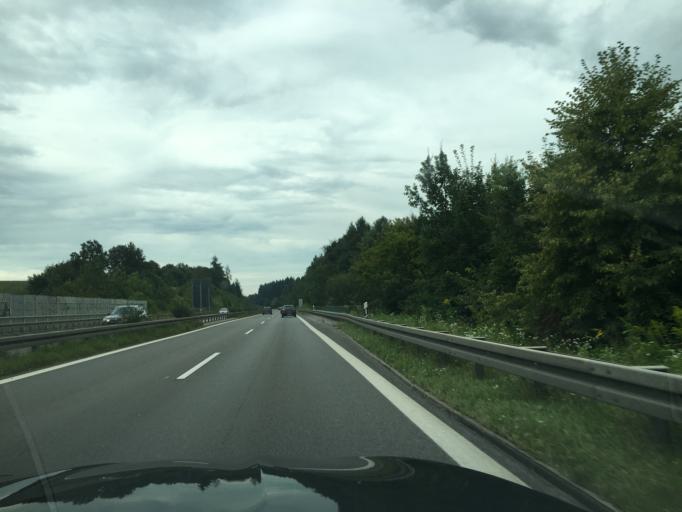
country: DE
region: Baden-Wuerttemberg
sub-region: Freiburg Region
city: Radolfzell am Bodensee
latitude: 47.7582
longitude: 8.9920
